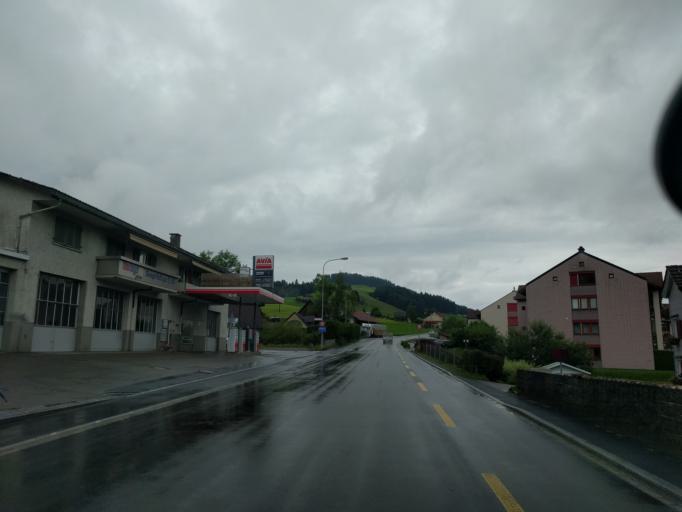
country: CH
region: Appenzell Ausserrhoden
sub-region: Bezirk Hinterland
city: Schwellbrunn
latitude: 47.3320
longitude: 9.2326
